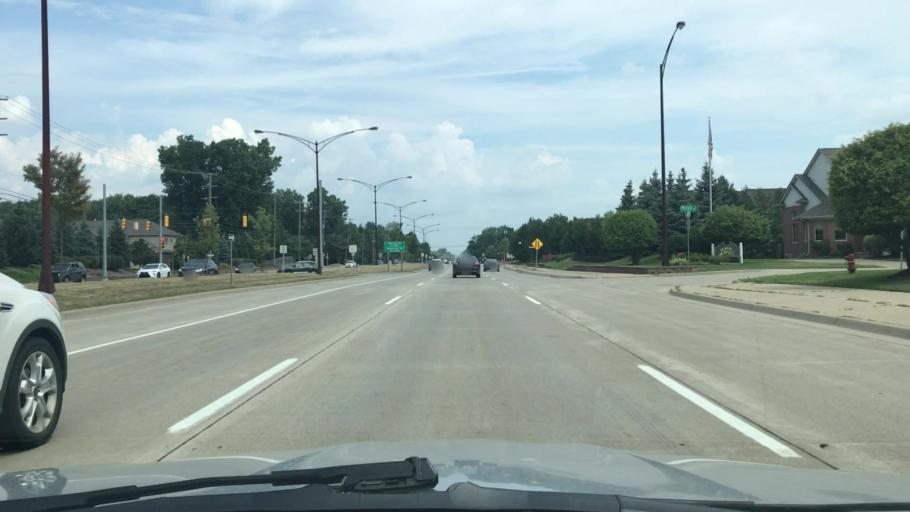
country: US
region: Michigan
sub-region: Oakland County
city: Troy
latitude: 42.5792
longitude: -83.1283
